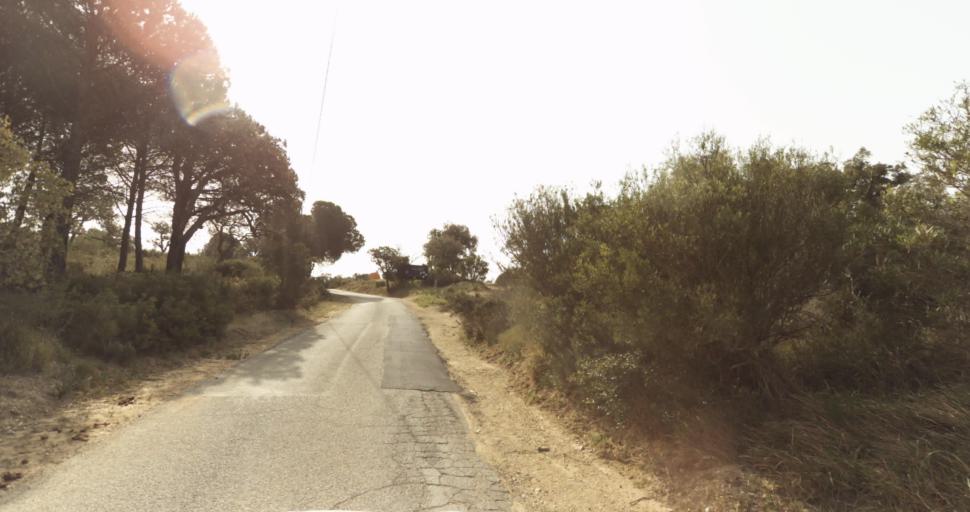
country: FR
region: Provence-Alpes-Cote d'Azur
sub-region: Departement du Var
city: Bormes-les-Mimosas
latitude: 43.1459
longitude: 6.3039
